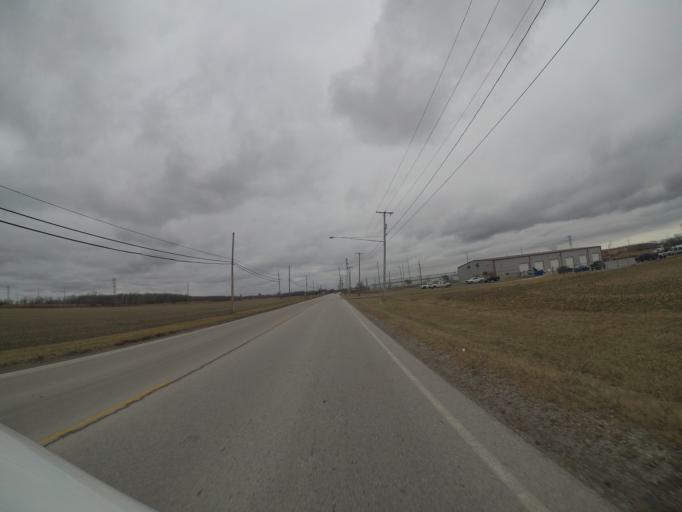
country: US
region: Ohio
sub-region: Wood County
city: Walbridge
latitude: 41.5899
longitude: -83.5126
